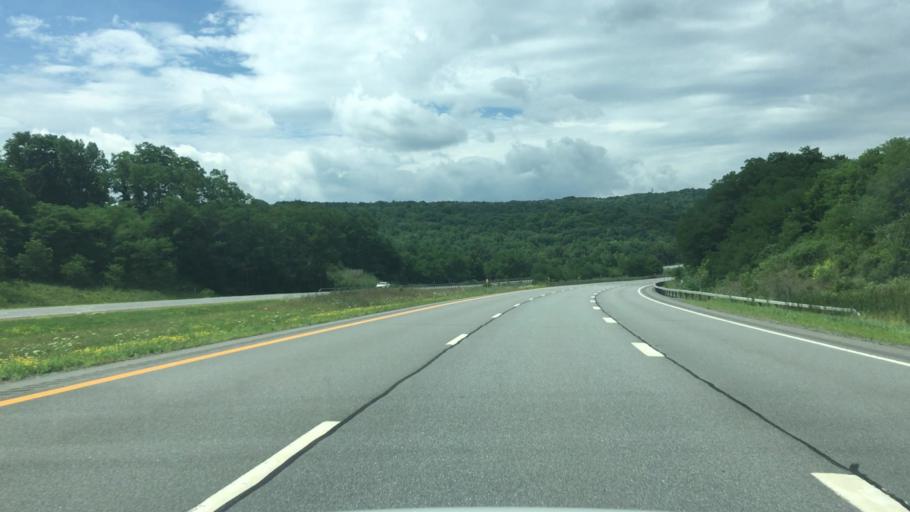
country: US
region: New York
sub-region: Albany County
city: Altamont
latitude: 42.7763
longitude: -74.0498
